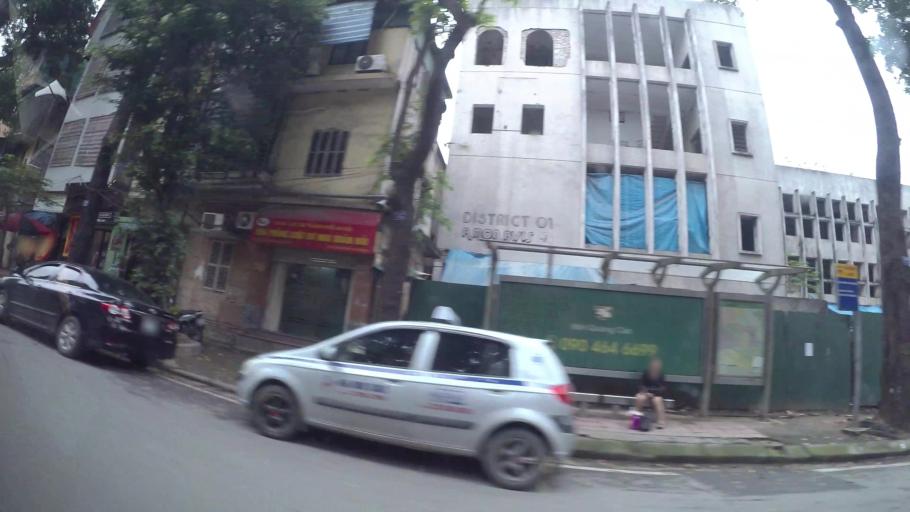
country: VN
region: Ha Noi
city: Hai BaTrung
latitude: 21.0144
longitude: 105.8598
